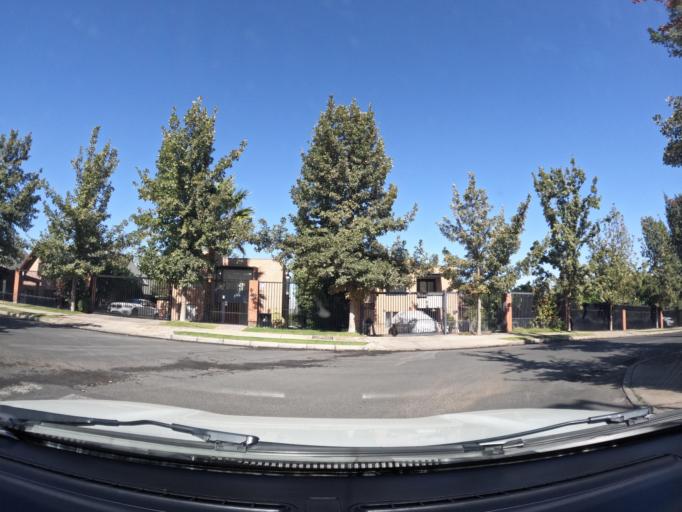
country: CL
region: Santiago Metropolitan
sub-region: Provincia de Santiago
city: Villa Presidente Frei, Nunoa, Santiago, Chile
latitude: -33.5022
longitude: -70.5265
